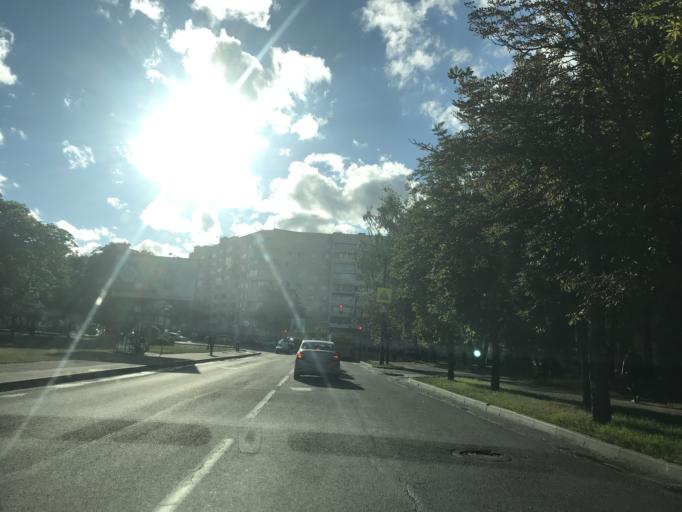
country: BY
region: Minsk
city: Minsk
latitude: 53.9497
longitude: 27.6178
